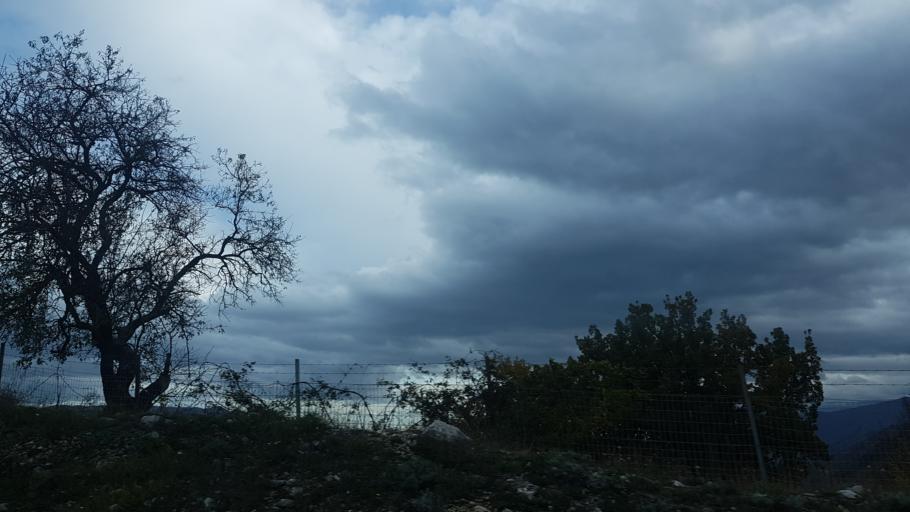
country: IT
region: Abruzzo
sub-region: Provincia dell' Aquila
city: Progetto Case Bazzano
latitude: 42.3677
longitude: 13.4307
